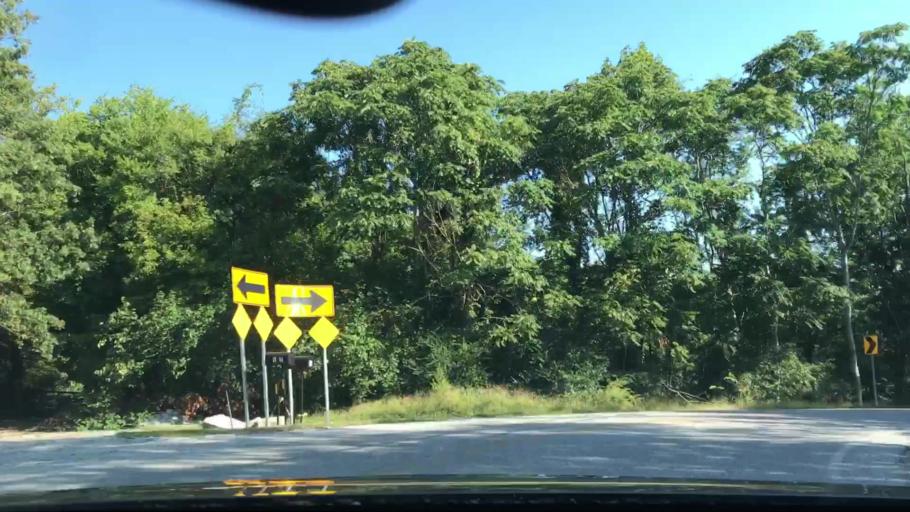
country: US
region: Tennessee
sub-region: Smith County
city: Carthage
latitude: 36.2725
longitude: -85.9577
